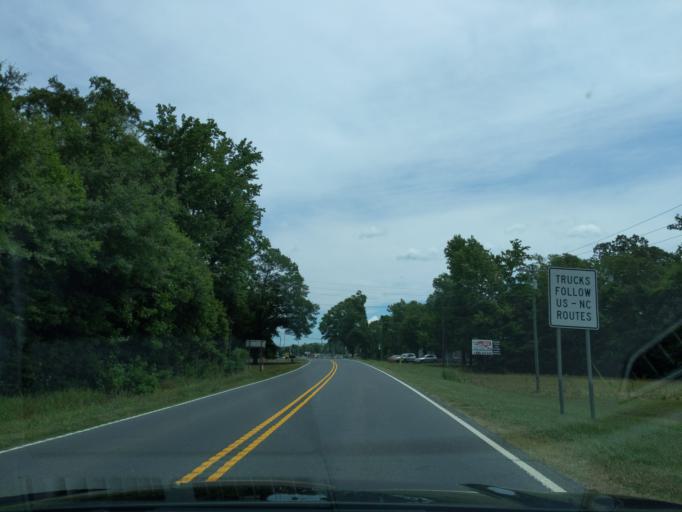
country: US
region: North Carolina
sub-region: Stanly County
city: Albemarle
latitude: 35.4700
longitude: -80.2710
